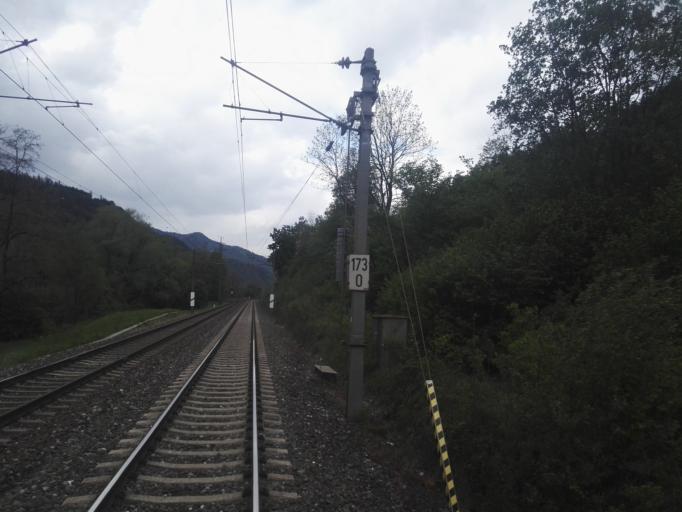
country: AT
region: Styria
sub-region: Politischer Bezirk Graz-Umgebung
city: Rothelstein
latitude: 47.3161
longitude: 15.3740
